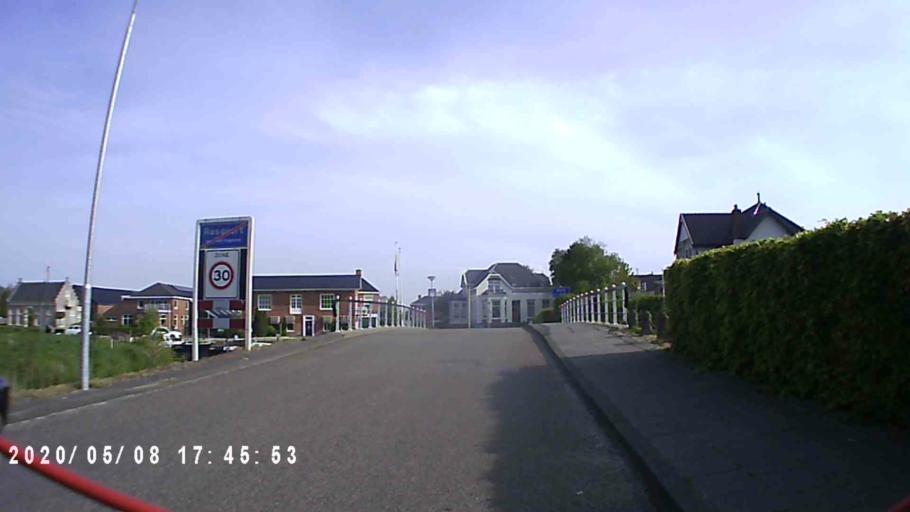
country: NL
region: Groningen
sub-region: Gemeente Winsum
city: Winsum
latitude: 53.3648
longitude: 6.5159
